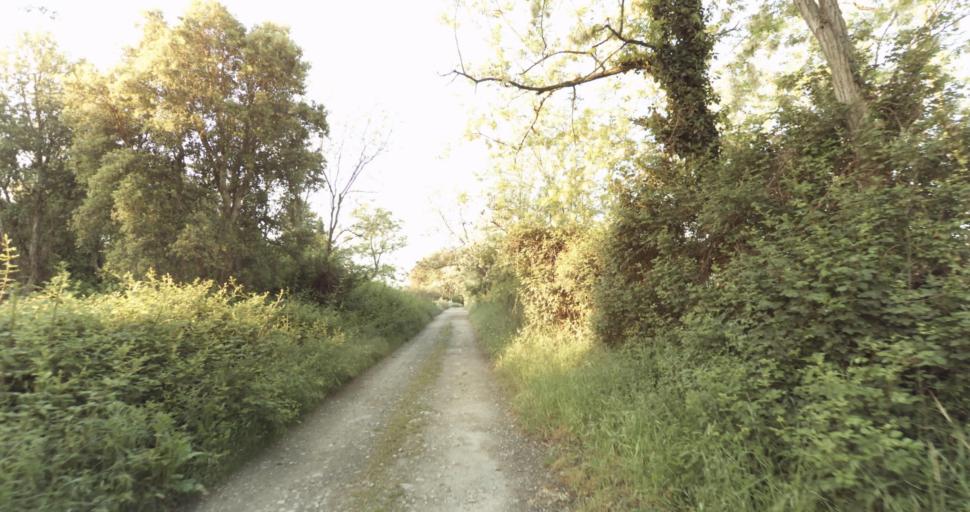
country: FR
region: Corsica
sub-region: Departement de la Haute-Corse
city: Biguglia
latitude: 42.6324
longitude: 9.4406
